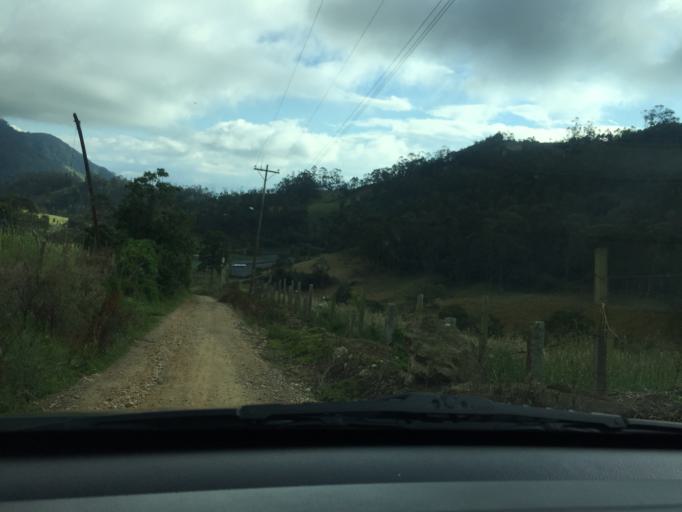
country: CO
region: Cundinamarca
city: Zipacon
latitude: 4.7455
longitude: -74.3719
